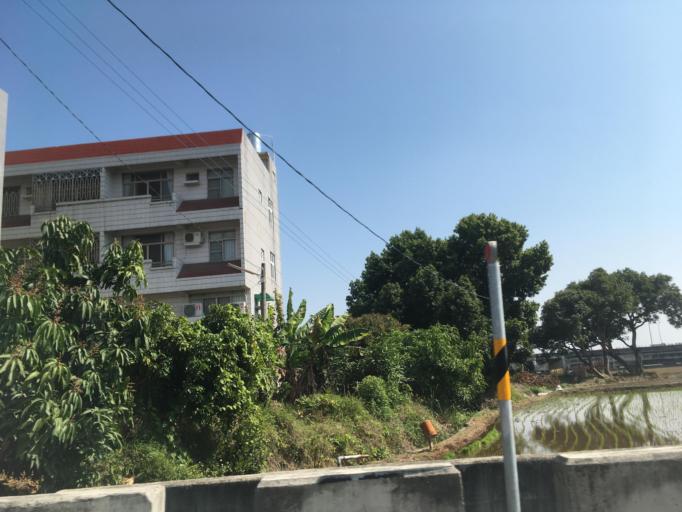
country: TW
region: Taiwan
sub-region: Chiayi
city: Jiayi Shi
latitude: 23.5523
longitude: 120.4132
